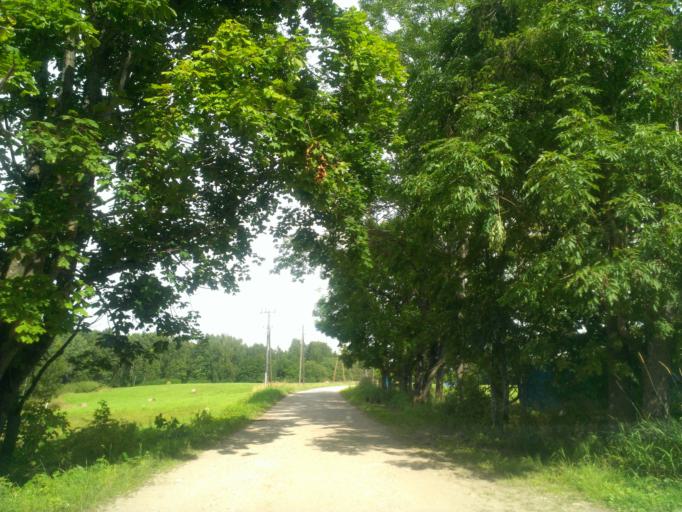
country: LV
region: Ligatne
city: Ligatne
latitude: 57.2245
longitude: 24.9628
